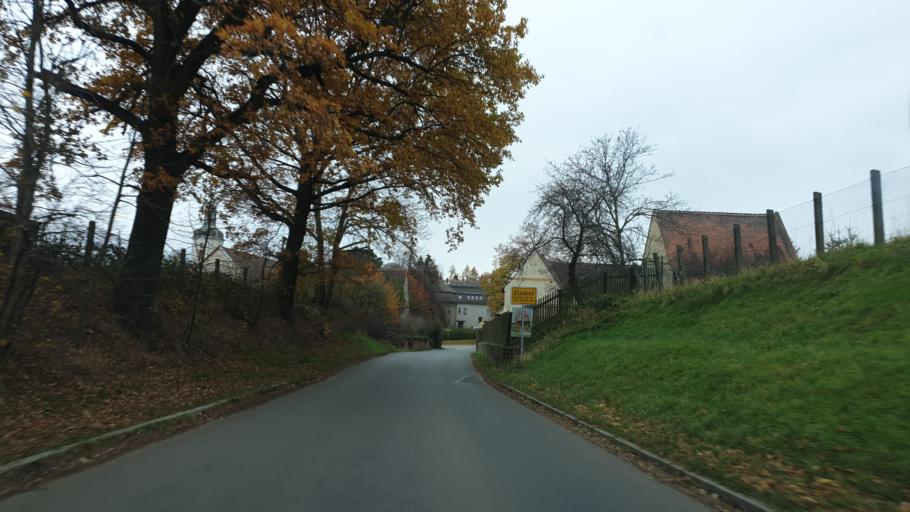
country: DE
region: Thuringia
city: Rauda
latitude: 50.9786
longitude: 11.9400
